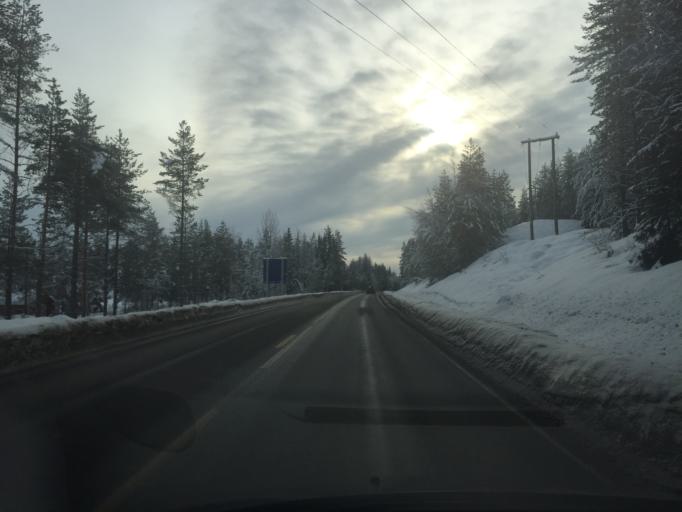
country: NO
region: Hedmark
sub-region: Trysil
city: Innbygda
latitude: 61.2875
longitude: 12.2788
